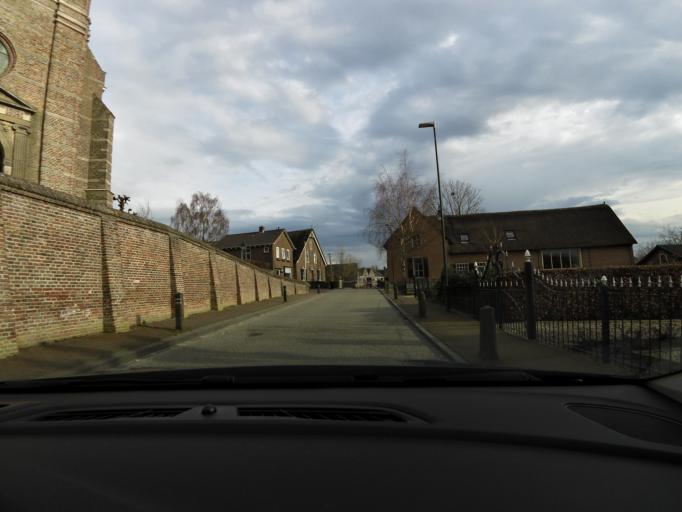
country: NL
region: South Holland
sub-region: Gemeente Gorinchem
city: Gorinchem
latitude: 51.8803
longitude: 4.9461
